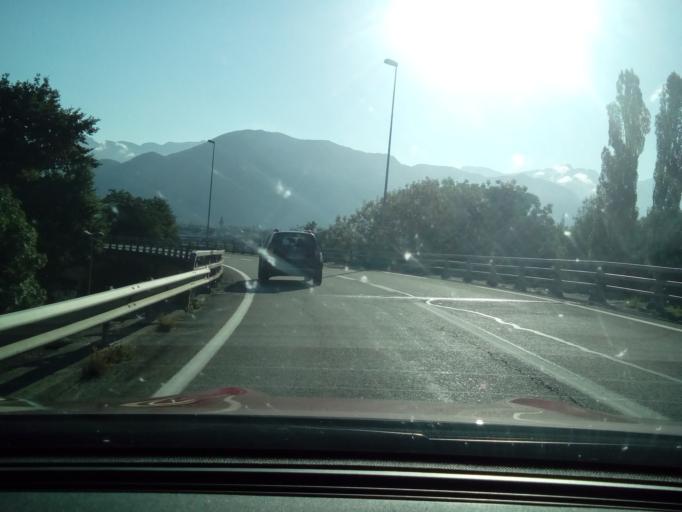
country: FR
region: Rhone-Alpes
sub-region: Departement de la Haute-Savoie
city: Cran-Gevrier
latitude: 45.8984
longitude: 6.1054
